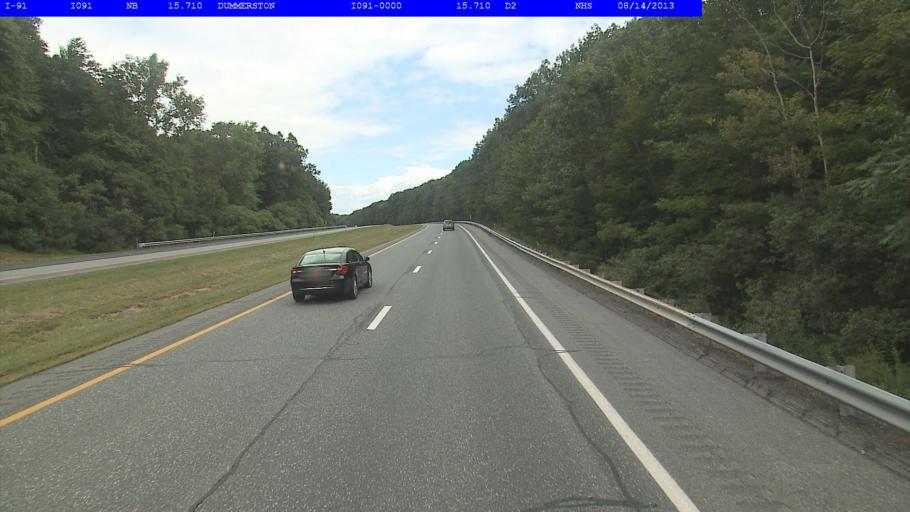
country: US
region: New Hampshire
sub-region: Cheshire County
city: Chesterfield
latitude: 42.9363
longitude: -72.5273
